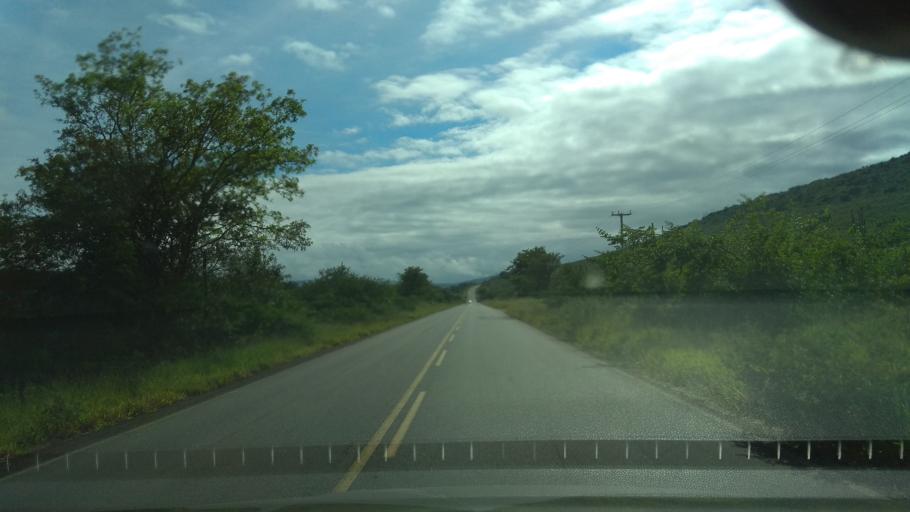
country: BR
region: Bahia
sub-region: Santa Ines
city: Santa Ines
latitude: -13.3608
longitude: -39.8821
